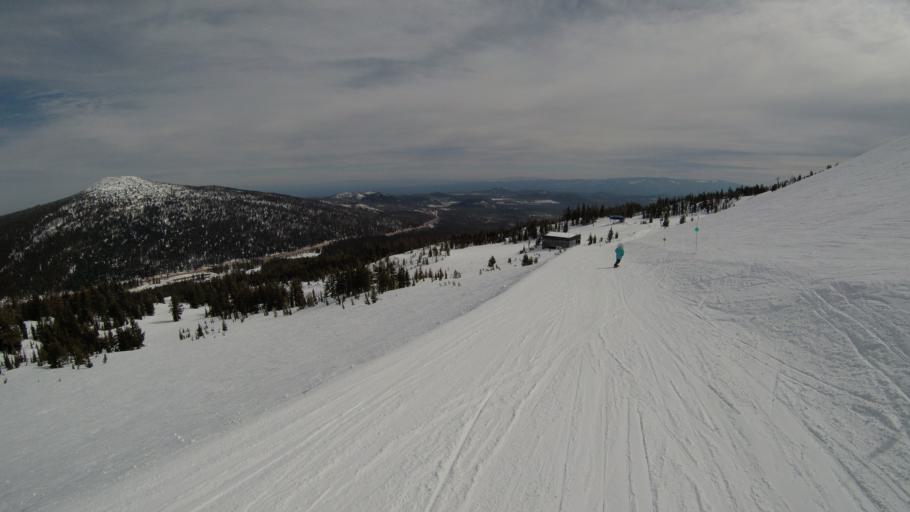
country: US
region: Oregon
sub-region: Deschutes County
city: Sunriver
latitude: 43.9889
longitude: -121.6827
